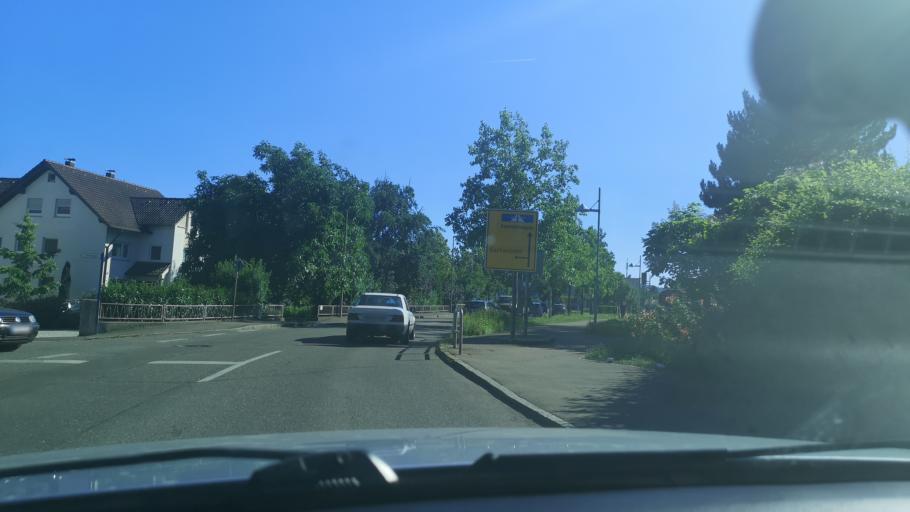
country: DE
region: Baden-Wuerttemberg
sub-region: Regierungsbezirk Stuttgart
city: Heiningen
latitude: 48.6591
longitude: 9.6519
